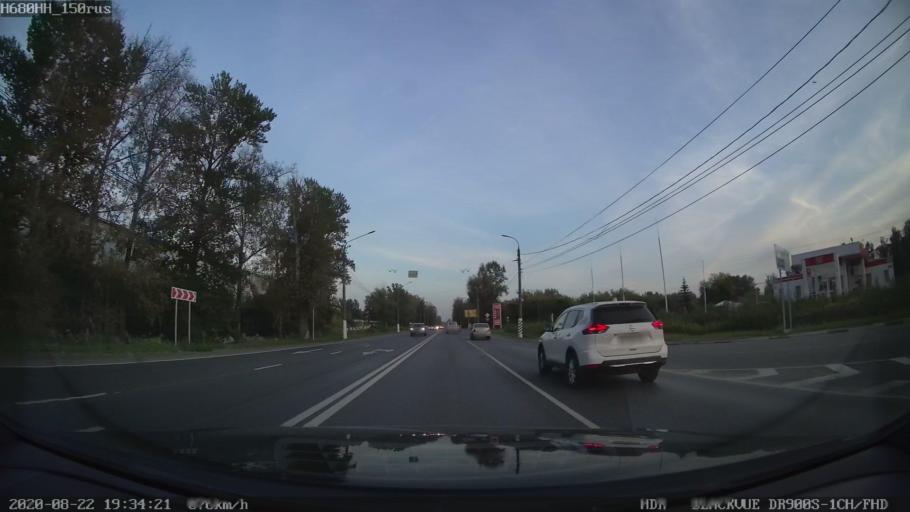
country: RU
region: Tverskaya
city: Tver
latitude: 56.8417
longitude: 35.9536
